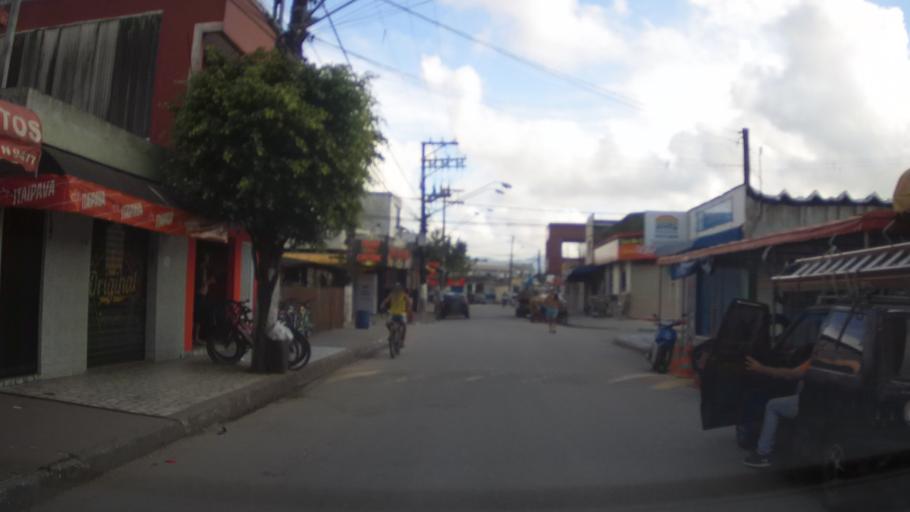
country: BR
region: Sao Paulo
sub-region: Praia Grande
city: Praia Grande
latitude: -24.0108
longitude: -46.4713
